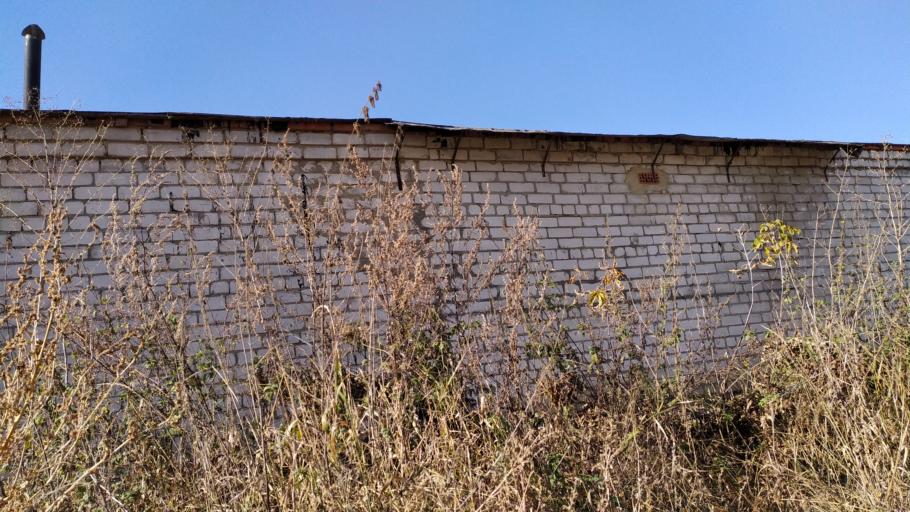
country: RU
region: Kursk
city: Kursk
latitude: 51.6512
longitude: 36.1528
